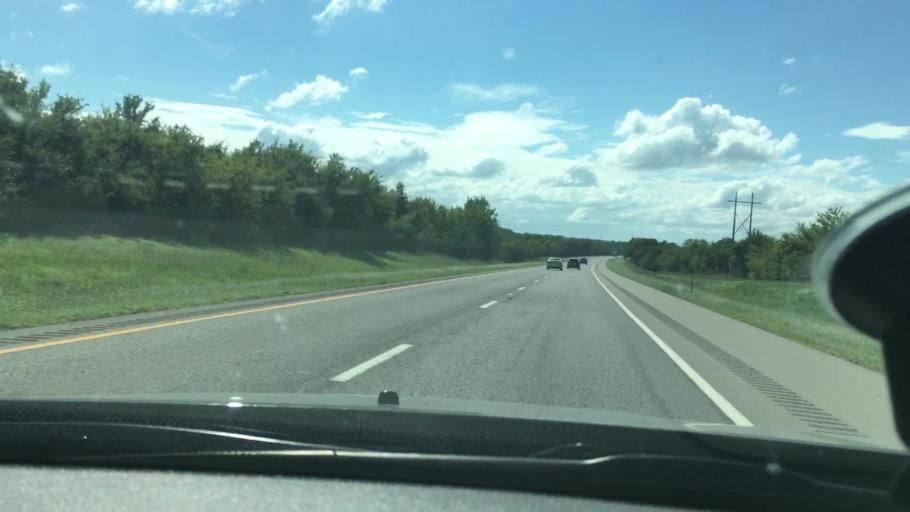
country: US
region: Oklahoma
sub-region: Muskogee County
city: Warner
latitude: 35.4593
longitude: -95.3895
